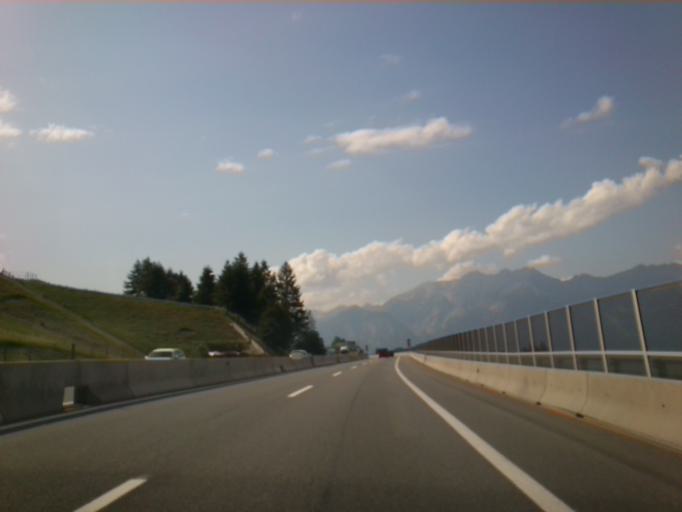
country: AT
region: Tyrol
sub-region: Politischer Bezirk Innsbruck Land
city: Schoenberg im Stubaital
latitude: 47.1809
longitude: 11.4116
